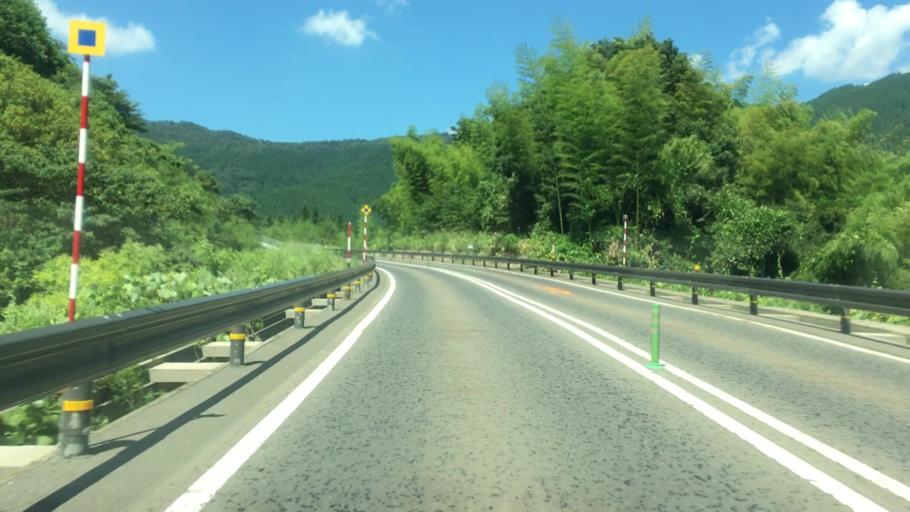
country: JP
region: Tottori
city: Tottori
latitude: 35.2808
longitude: 134.2258
